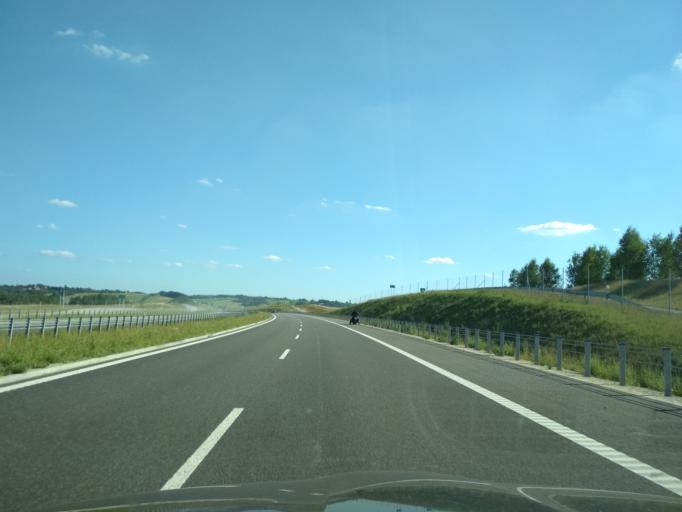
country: PL
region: Subcarpathian Voivodeship
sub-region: Rzeszow
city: Przybyszowka
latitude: 50.0579
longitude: 21.9239
